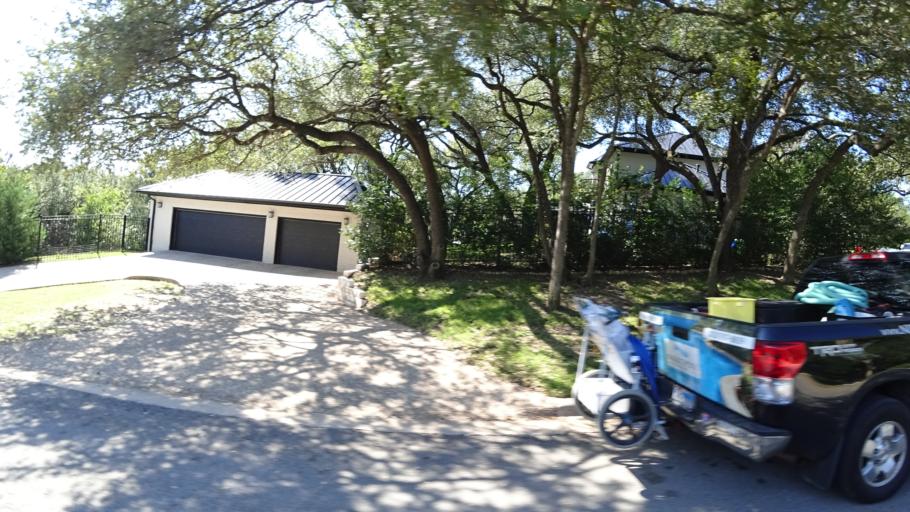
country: US
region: Texas
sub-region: Travis County
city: Rollingwood
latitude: 30.2826
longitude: -97.7921
